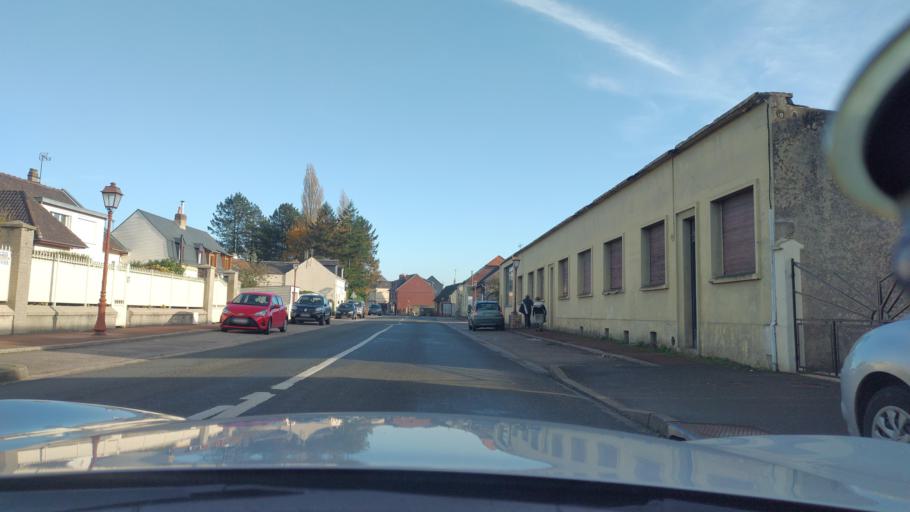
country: FR
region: Picardie
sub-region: Departement de la Somme
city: Fressenneville
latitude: 50.0678
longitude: 1.5713
